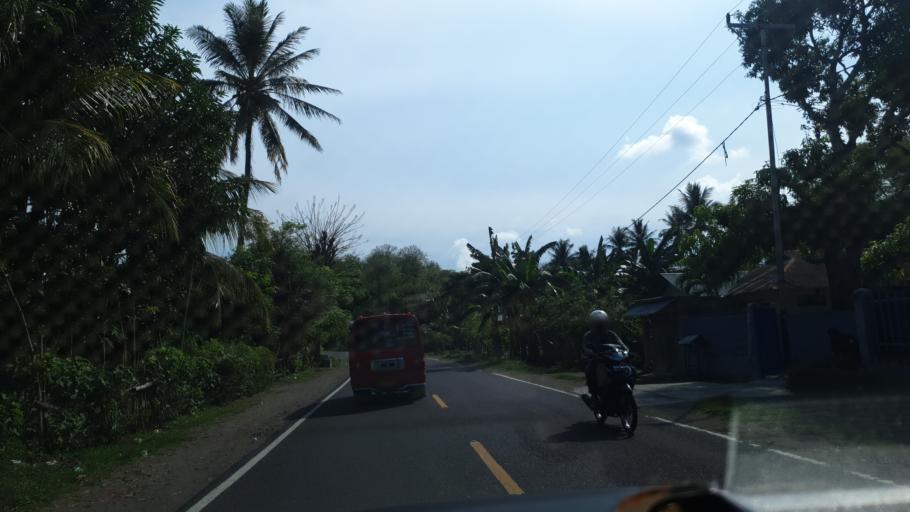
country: ID
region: East Nusa Tenggara
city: Nangalimang
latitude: -8.6415
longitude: 122.2065
